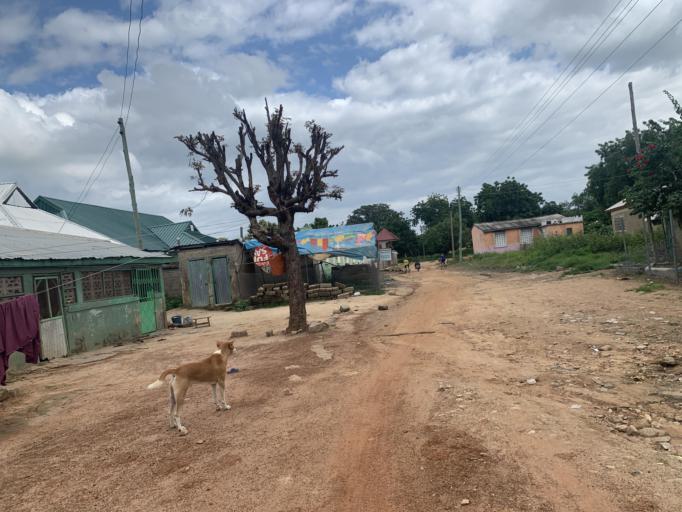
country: GH
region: Upper East
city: Navrongo
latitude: 10.9005
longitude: -1.0892
